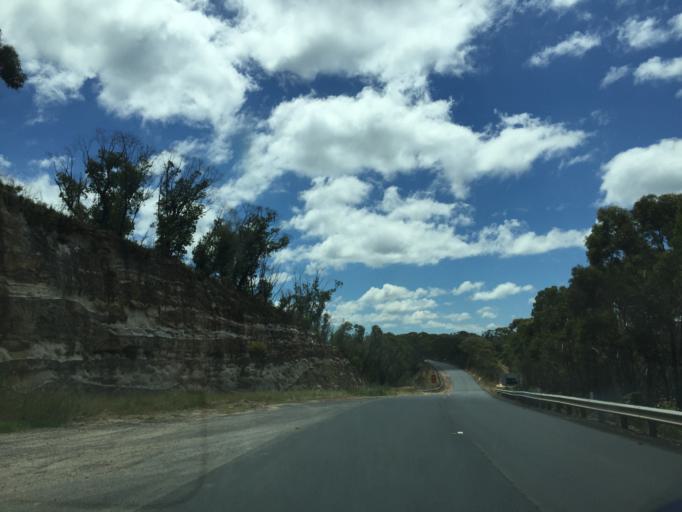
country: AU
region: New South Wales
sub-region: Blue Mountains Municipality
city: Blackheath
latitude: -33.5452
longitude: 150.3357
